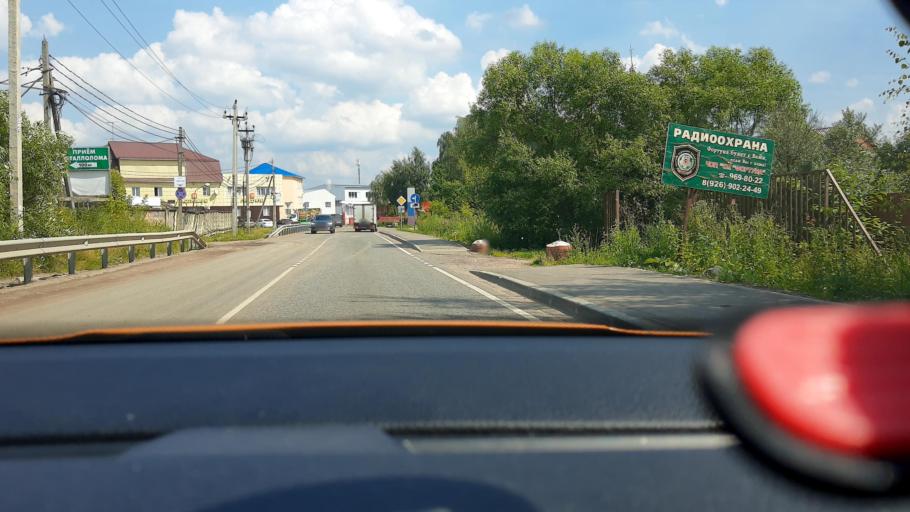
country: RU
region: Moskovskaya
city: Povedniki
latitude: 56.0078
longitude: 37.5835
